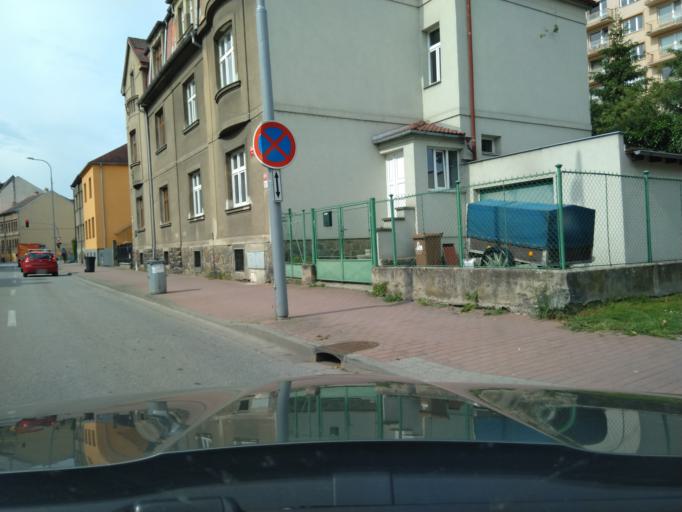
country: CZ
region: Jihocesky
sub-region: Okres Ceske Budejovice
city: Ceske Budejovice
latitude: 48.9841
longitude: 14.4779
